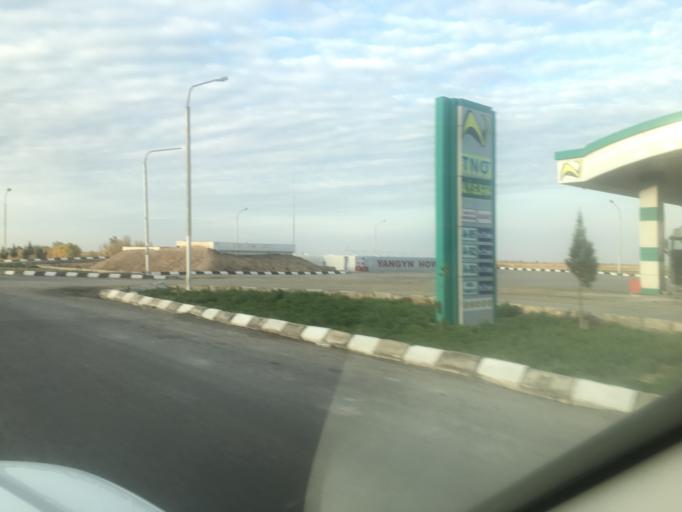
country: TM
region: Ahal
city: Tejen
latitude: 37.3470
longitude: 60.7344
